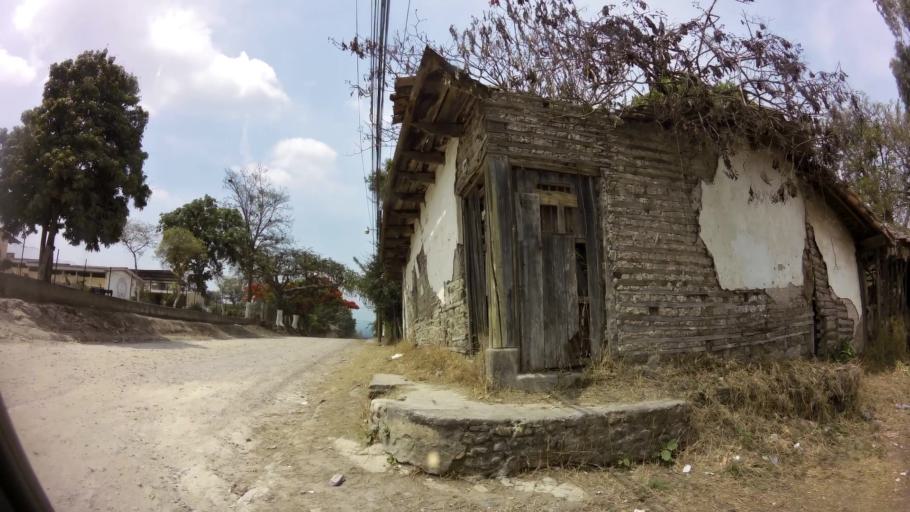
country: HN
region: Comayagua
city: Siguatepeque
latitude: 14.6007
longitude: -87.8294
